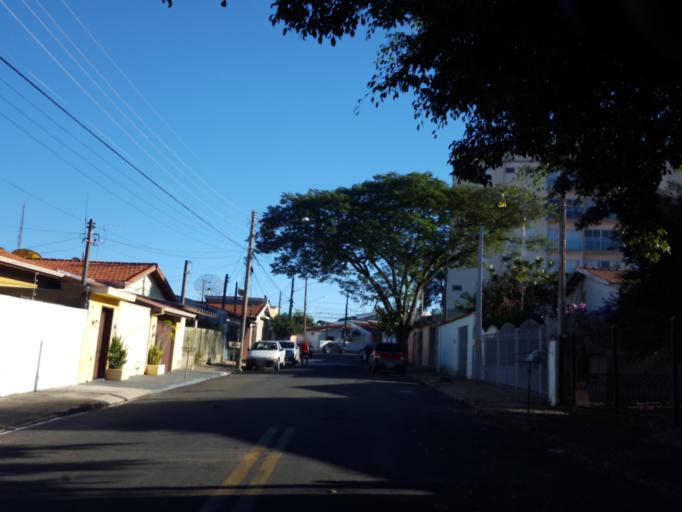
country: BR
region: Sao Paulo
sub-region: Indaiatuba
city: Indaiatuba
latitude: -23.0742
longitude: -47.2011
